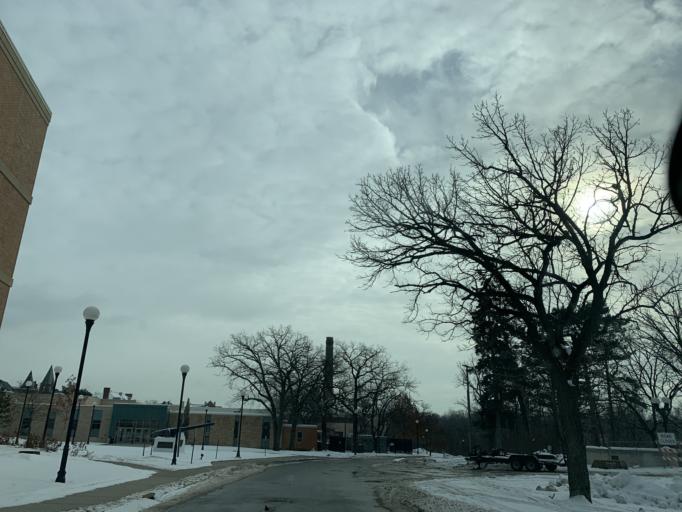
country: US
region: Minnesota
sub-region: Dakota County
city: Mendota Heights
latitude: 44.9135
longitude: -93.2057
